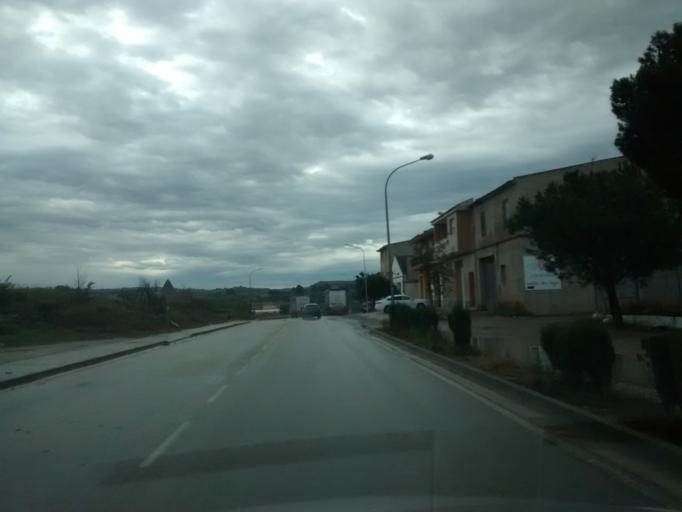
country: ES
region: Aragon
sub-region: Provincia de Zaragoza
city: Maella
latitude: 41.1256
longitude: 0.1350
